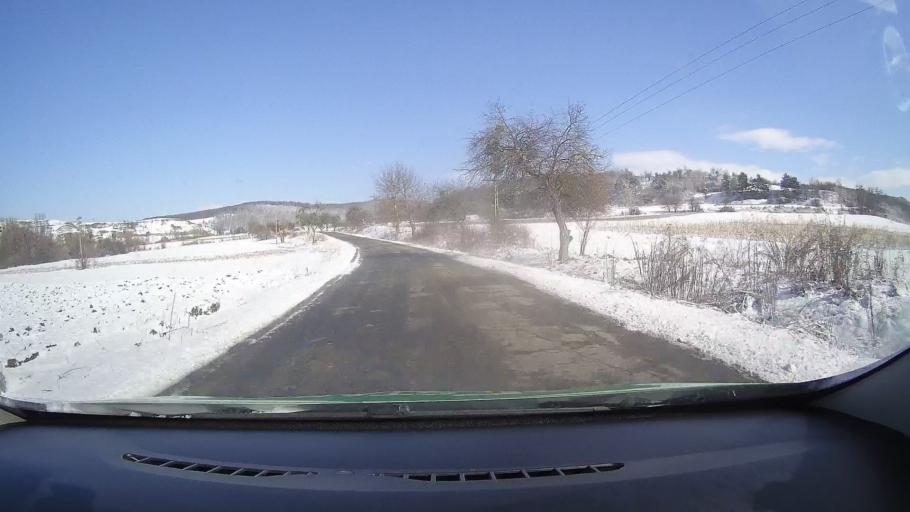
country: RO
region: Sibiu
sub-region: Comuna Mihaileni
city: Mihaileni
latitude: 46.0163
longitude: 24.3848
